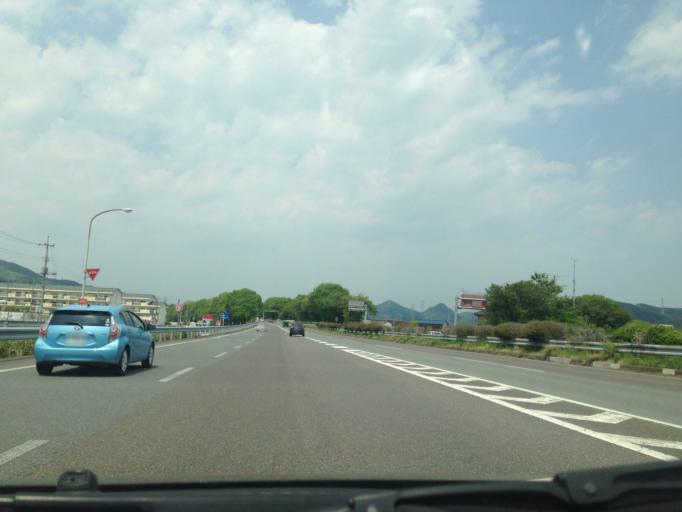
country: JP
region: Tochigi
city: Utsunomiya-shi
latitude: 36.6370
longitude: 139.8454
